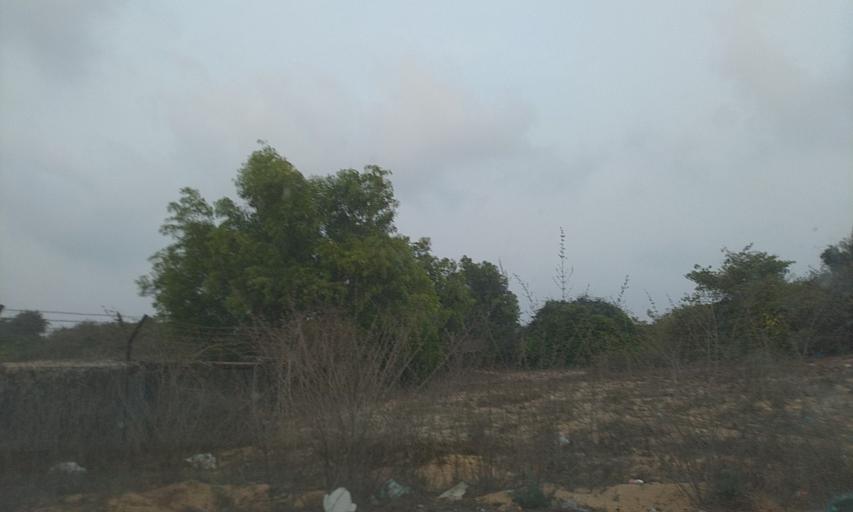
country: IN
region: Goa
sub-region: South Goa
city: Cavelossim
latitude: 15.1894
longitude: 73.9419
